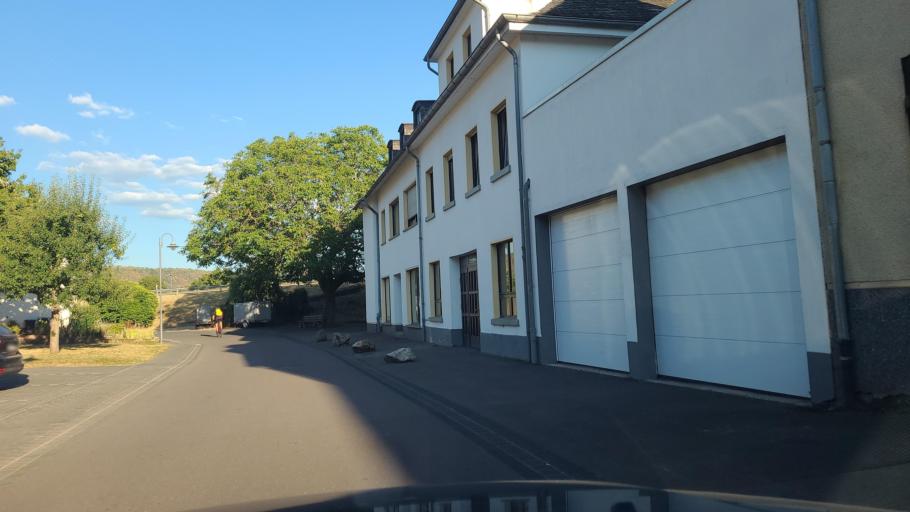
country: DE
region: Rheinland-Pfalz
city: Klusserath
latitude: 49.8429
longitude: 6.8498
